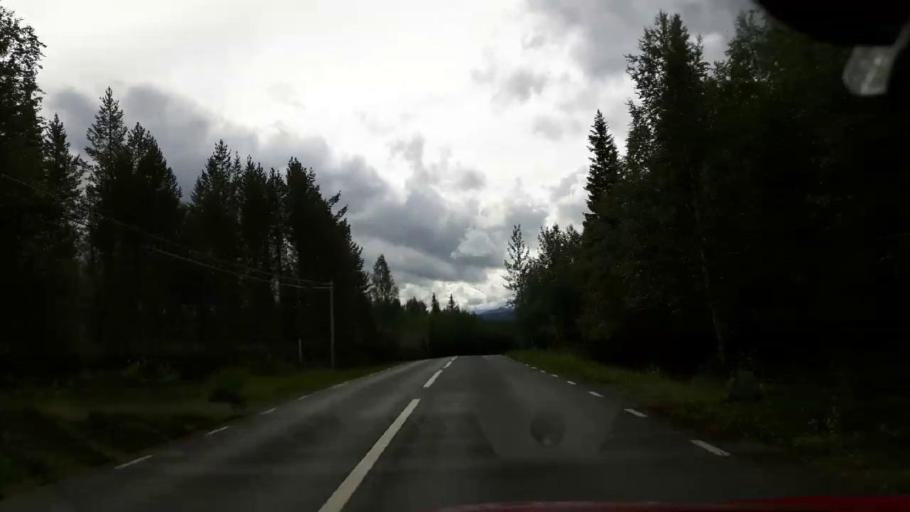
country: NO
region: Nord-Trondelag
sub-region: Lierne
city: Sandvika
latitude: 64.5194
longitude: 14.1625
